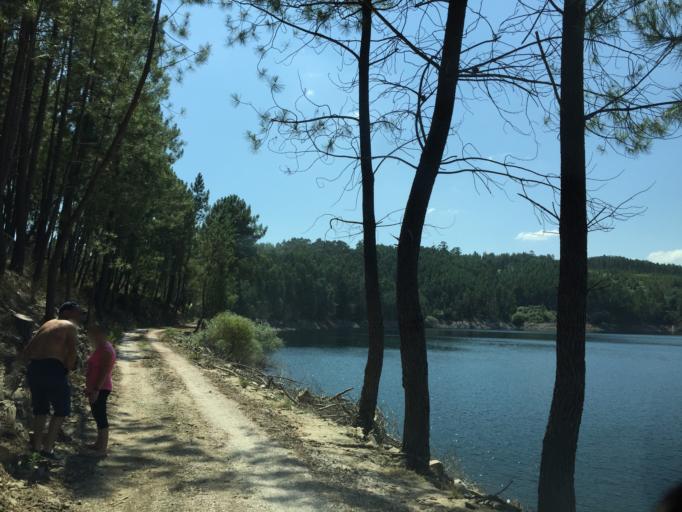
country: PT
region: Leiria
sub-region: Pedrogao Grande
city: Pedrogao Grande
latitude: 39.9318
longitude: -8.1210
